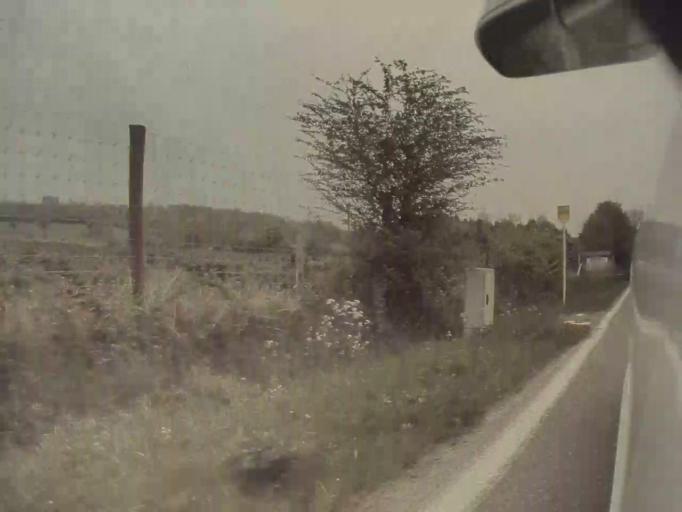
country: BE
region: Wallonia
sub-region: Province du Luxembourg
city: Durbuy
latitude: 50.3767
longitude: 5.4681
